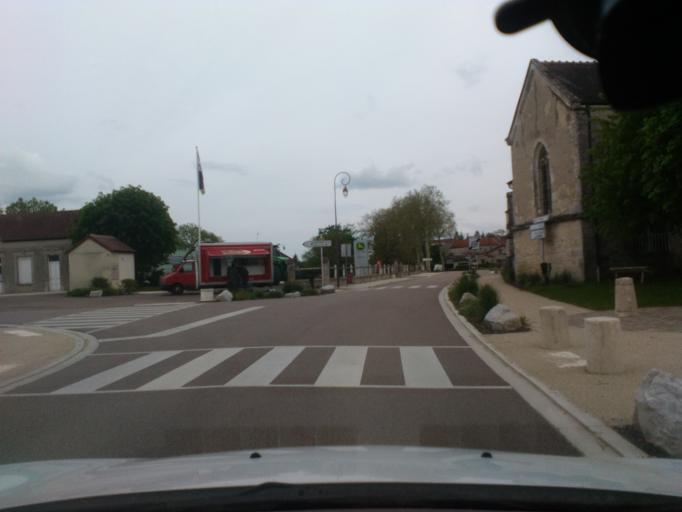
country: FR
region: Champagne-Ardenne
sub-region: Departement de l'Aube
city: Bar-sur-Aube
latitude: 48.2238
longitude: 4.8079
